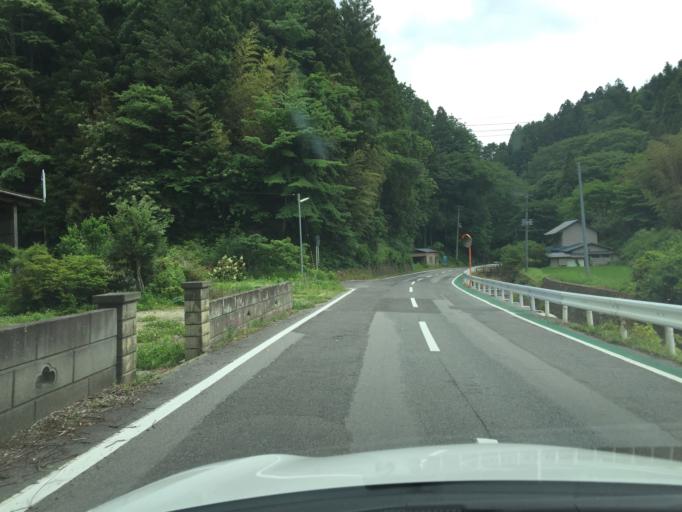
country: JP
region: Fukushima
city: Miharu
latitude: 37.2989
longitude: 140.5411
